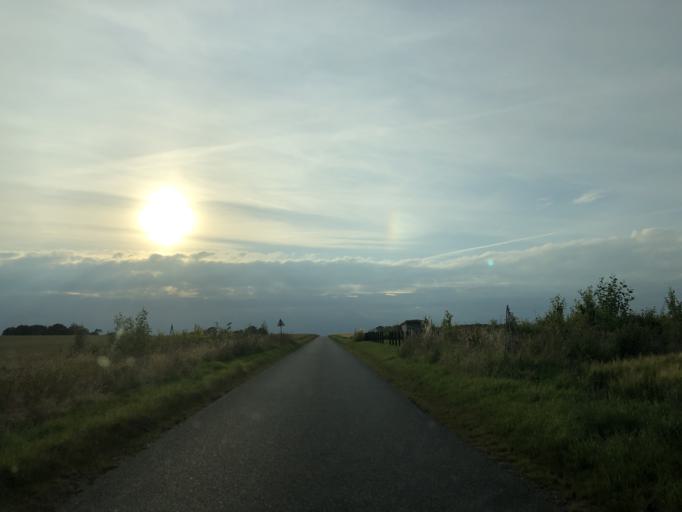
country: DK
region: South Denmark
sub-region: Fredericia Kommune
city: Taulov
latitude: 55.5935
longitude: 9.6142
